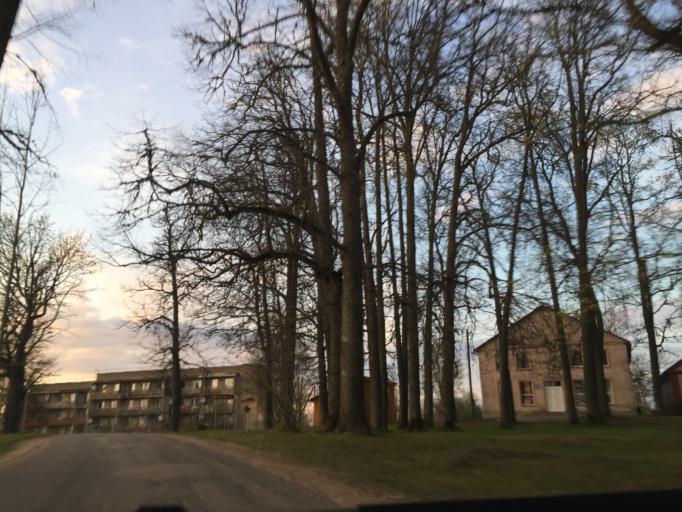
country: LV
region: Aluksnes Rajons
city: Aluksne
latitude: 57.2743
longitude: 26.9270
